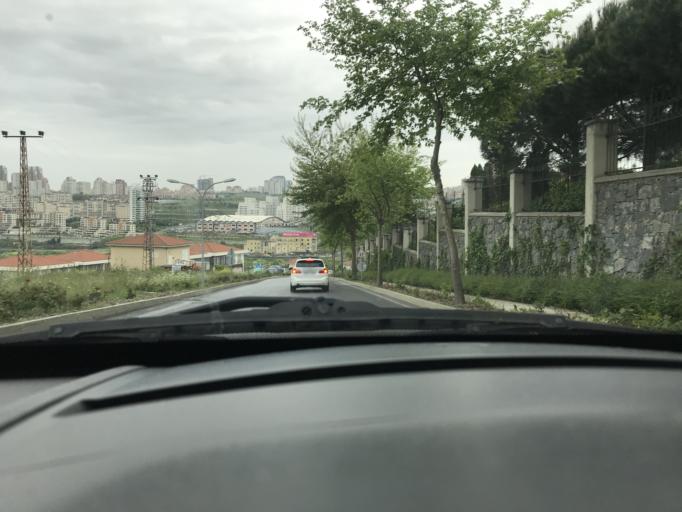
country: TR
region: Istanbul
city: Esenyurt
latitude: 41.0874
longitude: 28.6822
